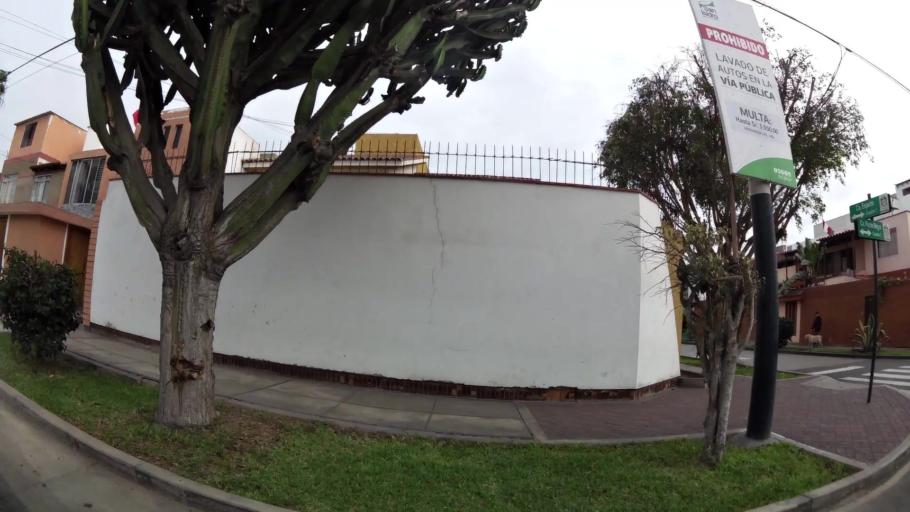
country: PE
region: Lima
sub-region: Lima
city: San Isidro
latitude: -12.1067
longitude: -77.0564
